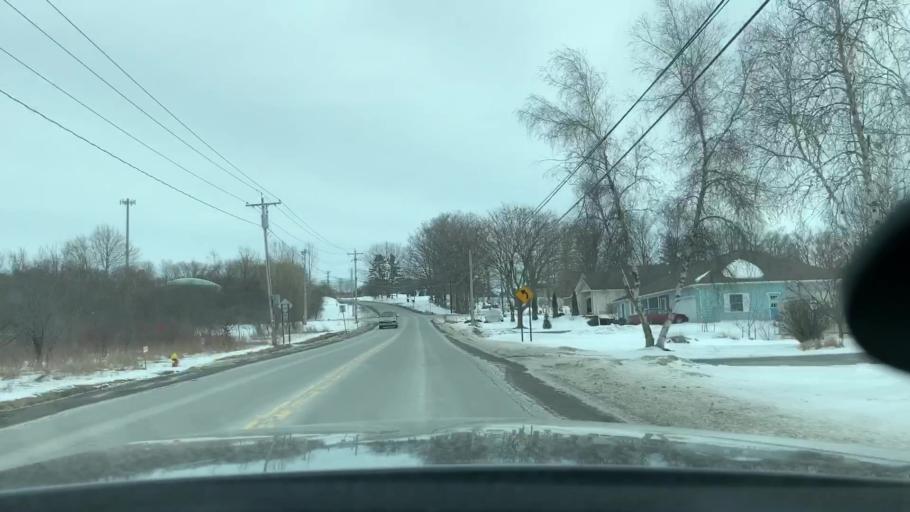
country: US
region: New York
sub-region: Oneida County
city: Washington Mills
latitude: 43.0527
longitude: -75.2421
